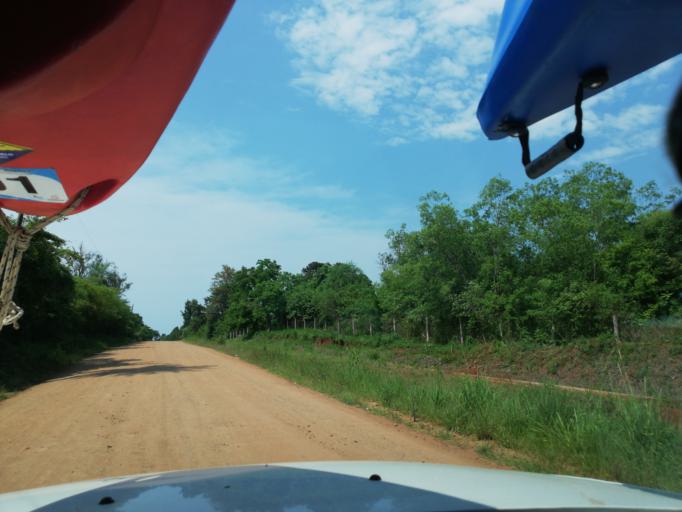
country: AR
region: Misiones
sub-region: Departamento de San Ignacio
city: San Ignacio
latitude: -27.2636
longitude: -55.5494
